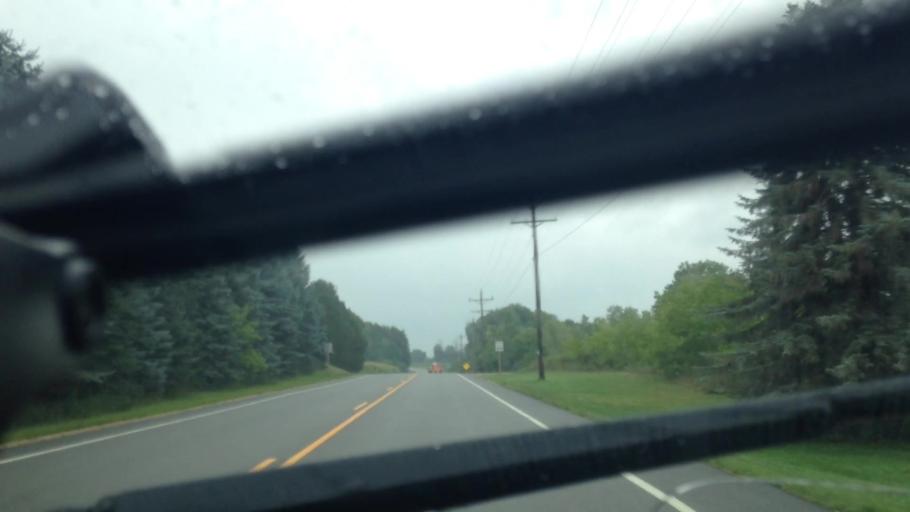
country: US
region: Wisconsin
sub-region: Washington County
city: Slinger
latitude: 43.3186
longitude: -88.2666
